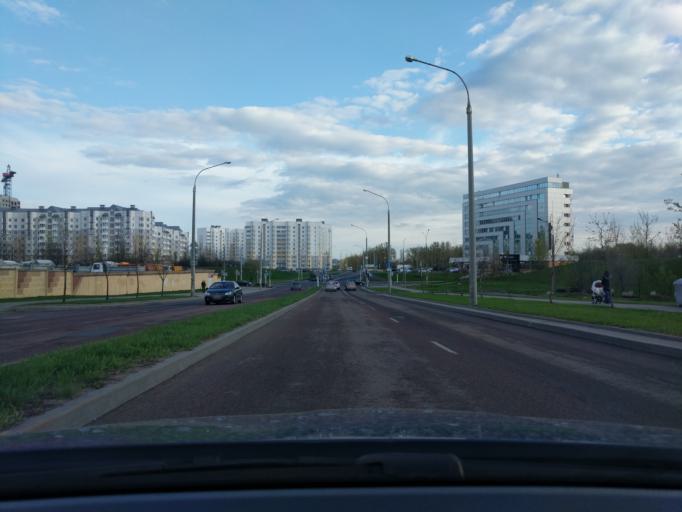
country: BY
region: Minsk
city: Novoye Medvezhino
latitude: 53.9028
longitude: 27.4735
